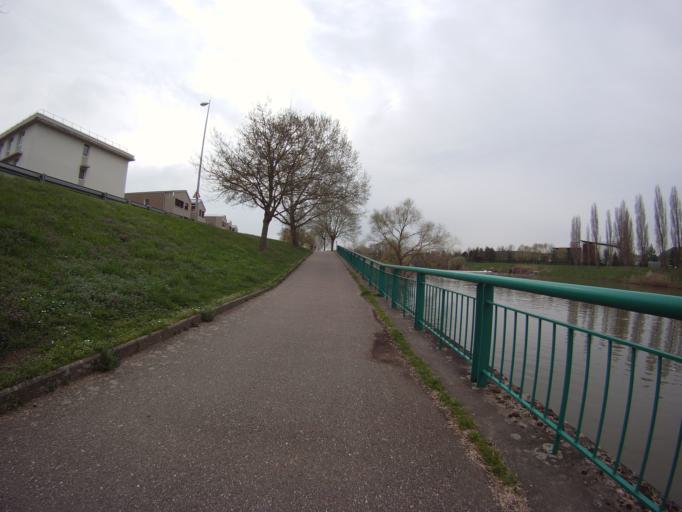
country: FR
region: Lorraine
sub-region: Departement de Meurthe-et-Moselle
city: Malzeville
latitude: 48.7147
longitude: 6.1745
